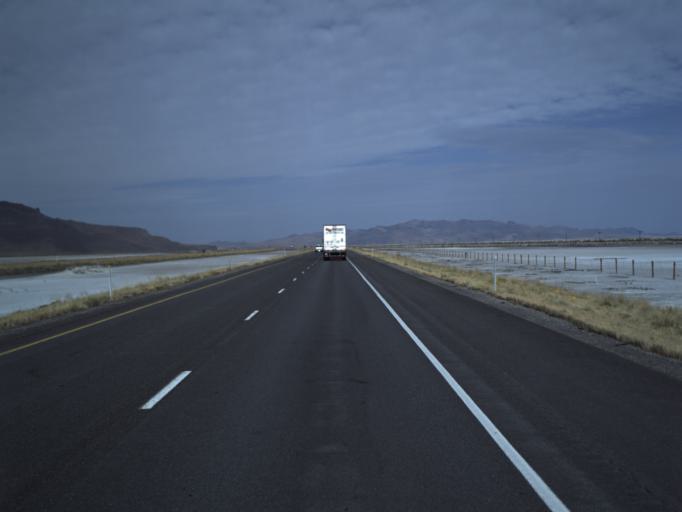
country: US
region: Utah
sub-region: Tooele County
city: Grantsville
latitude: 40.7161
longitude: -112.5442
